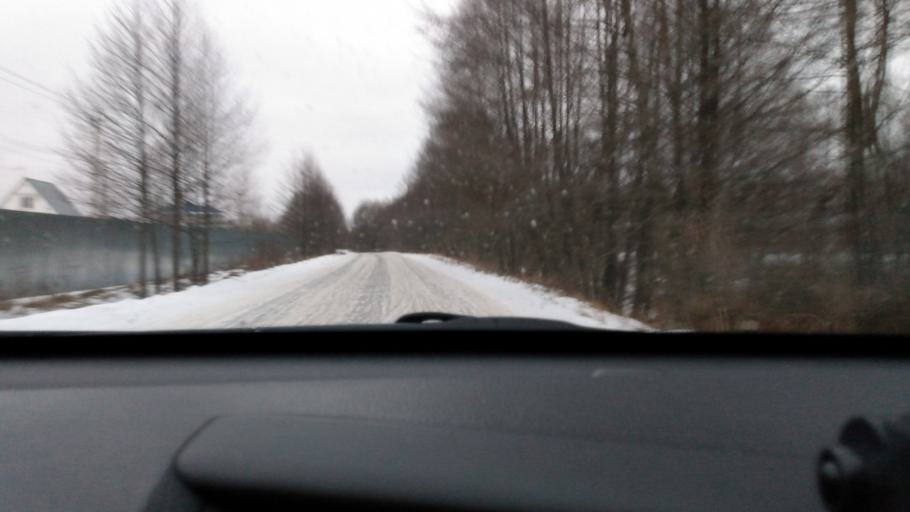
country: RU
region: Moskovskaya
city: Meshcherino
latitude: 55.3149
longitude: 38.3335
